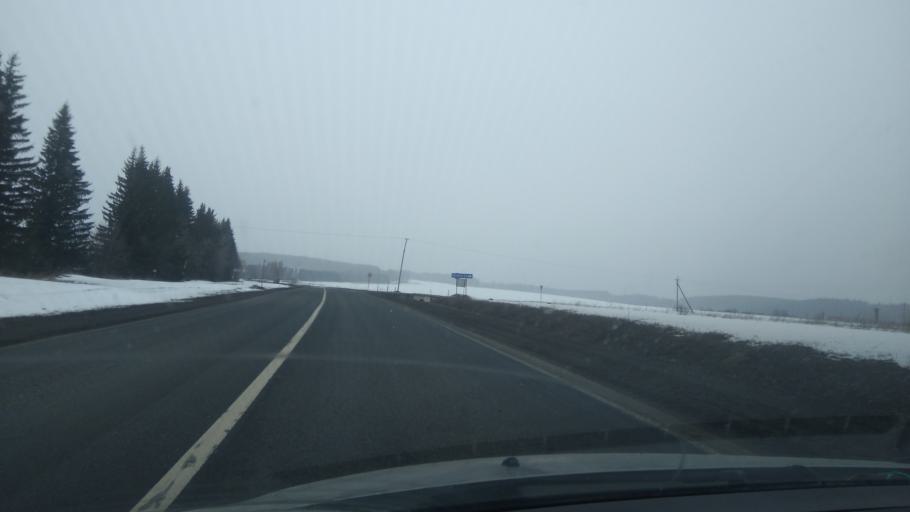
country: RU
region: Perm
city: Suksun
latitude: 57.0689
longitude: 57.4207
